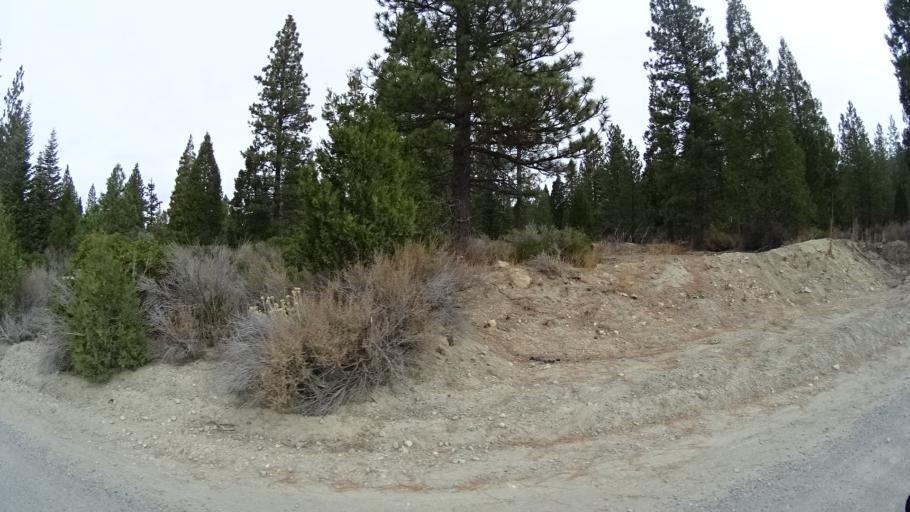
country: US
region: California
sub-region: Siskiyou County
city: Weed
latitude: 41.3933
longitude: -122.3684
